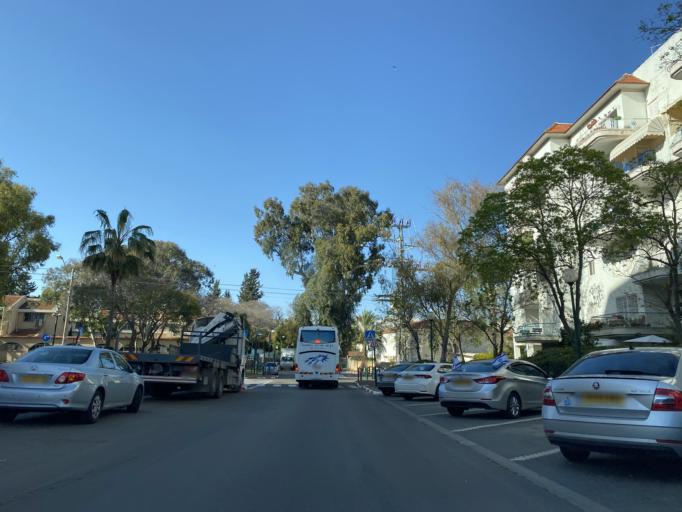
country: IL
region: Central District
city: Kfar Saba
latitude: 32.1803
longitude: 34.9159
